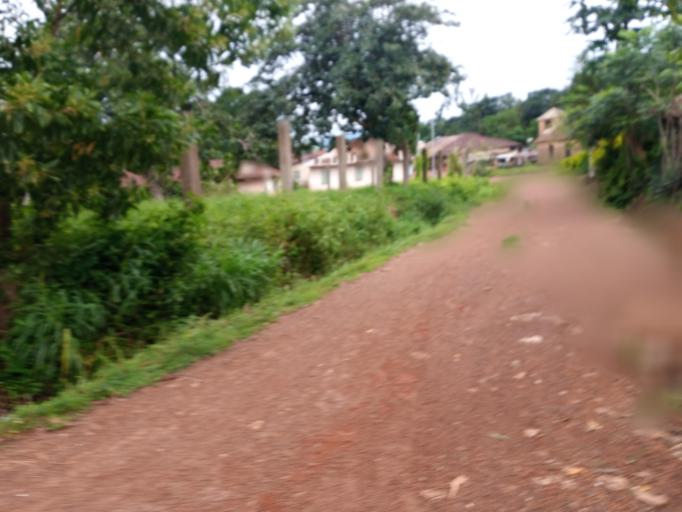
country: SL
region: Southern Province
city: Largo
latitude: 8.2032
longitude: -12.0604
